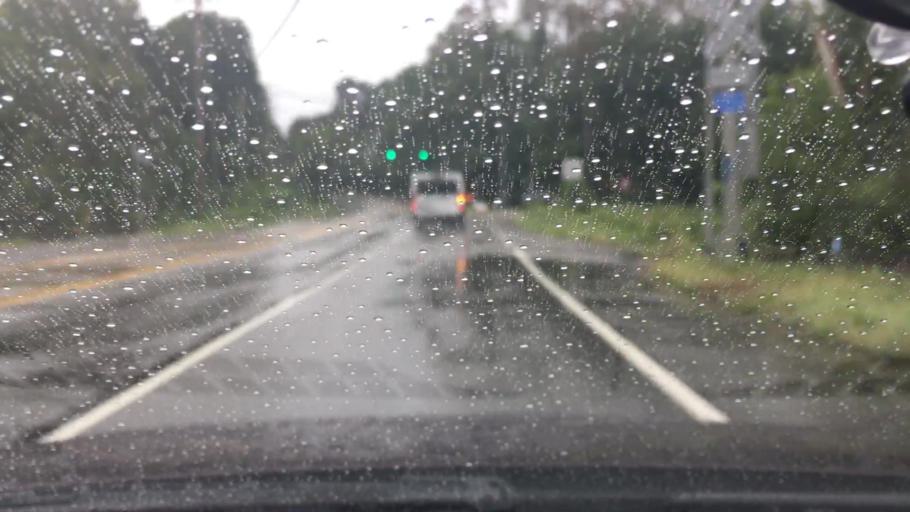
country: US
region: New York
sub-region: Dutchess County
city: Hillside Lake
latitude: 41.5756
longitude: -73.8209
